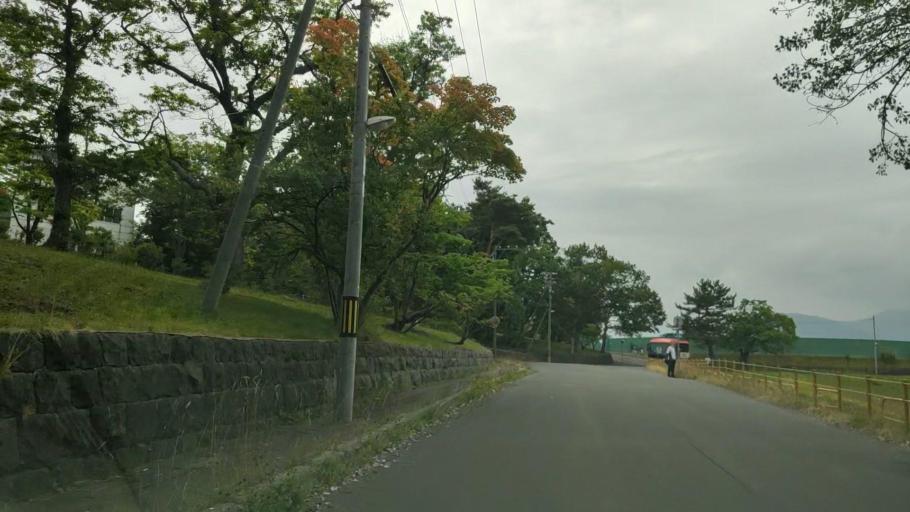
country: JP
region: Hokkaido
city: Otaru
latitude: 43.1880
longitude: 140.9921
